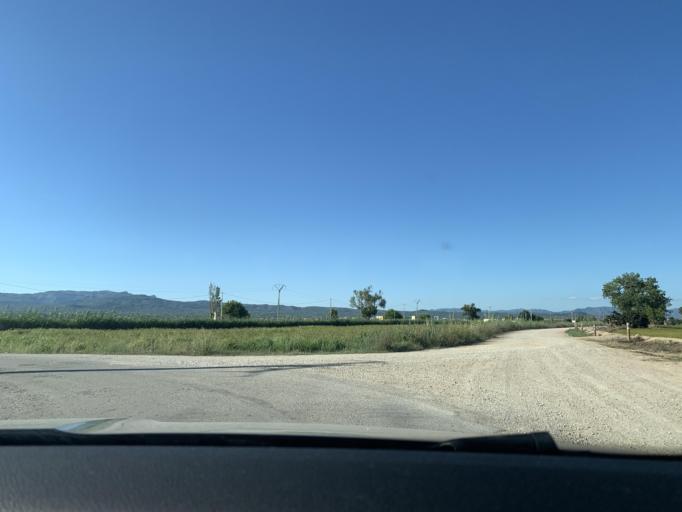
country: ES
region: Catalonia
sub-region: Provincia de Tarragona
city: L'Ampolla
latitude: 40.7706
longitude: 0.7098
